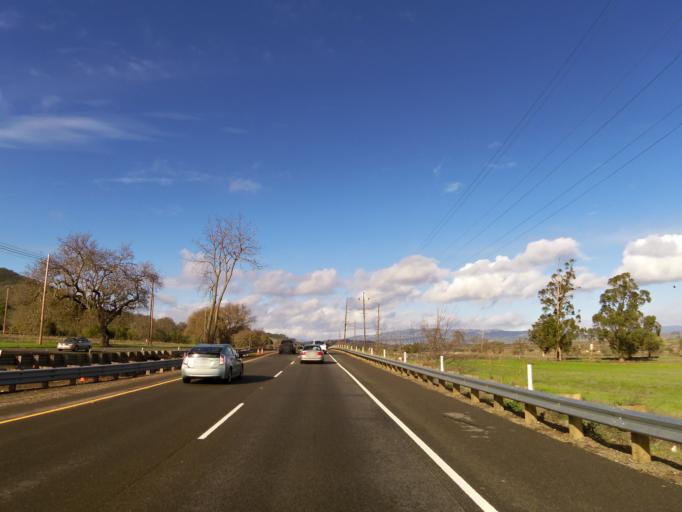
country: US
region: California
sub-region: Marin County
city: Novato
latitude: 38.1539
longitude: -122.5675
